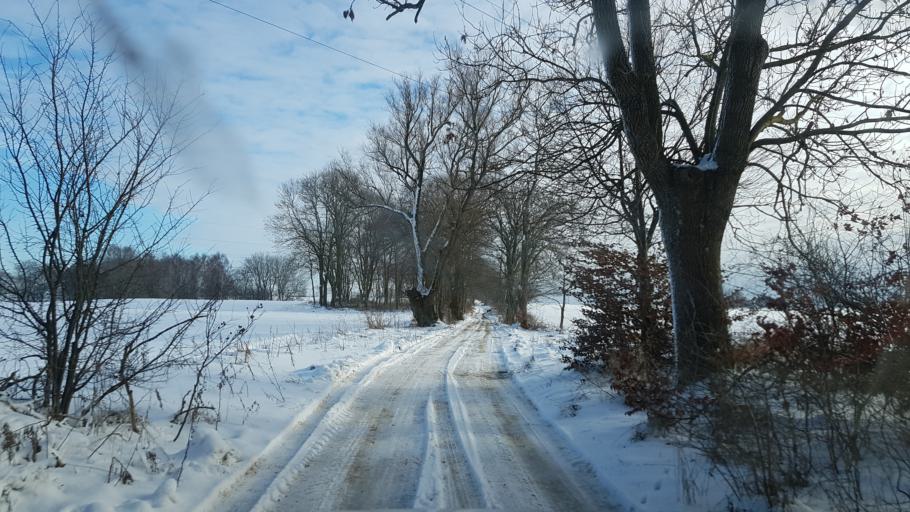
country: PL
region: West Pomeranian Voivodeship
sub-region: Powiat drawski
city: Drawsko Pomorskie
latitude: 53.5349
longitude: 15.7744
